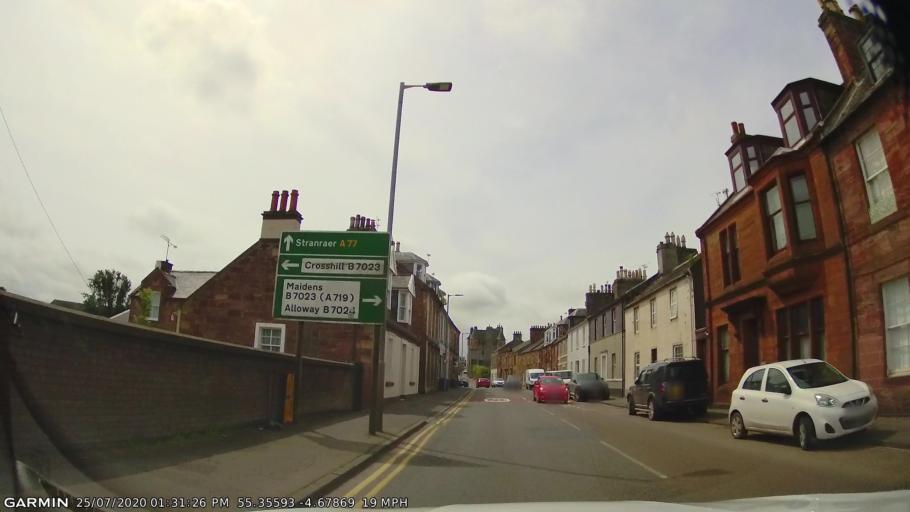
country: GB
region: Scotland
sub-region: South Ayrshire
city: Maybole
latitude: 55.3559
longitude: -4.6787
